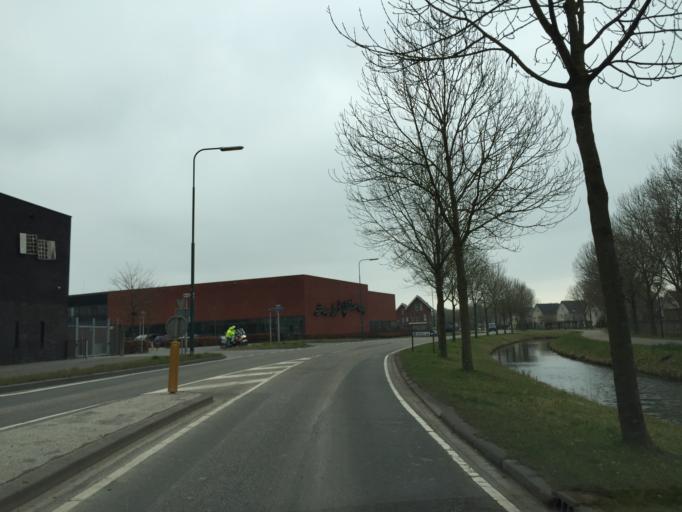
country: NL
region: Utrecht
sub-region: Stichtse Vecht
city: Spechtenkamp
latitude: 52.0903
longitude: 5.0235
